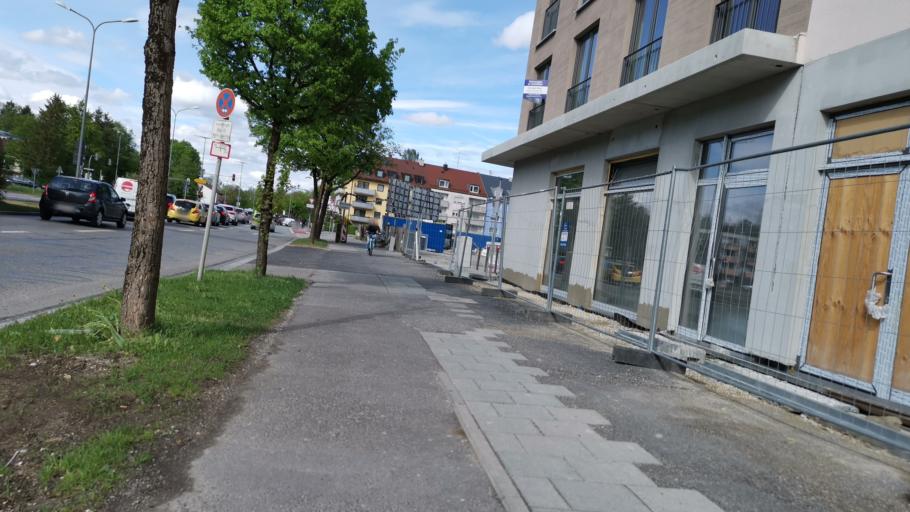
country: DE
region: Bavaria
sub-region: Upper Bavaria
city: Pullach im Isartal
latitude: 48.0972
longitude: 11.5079
